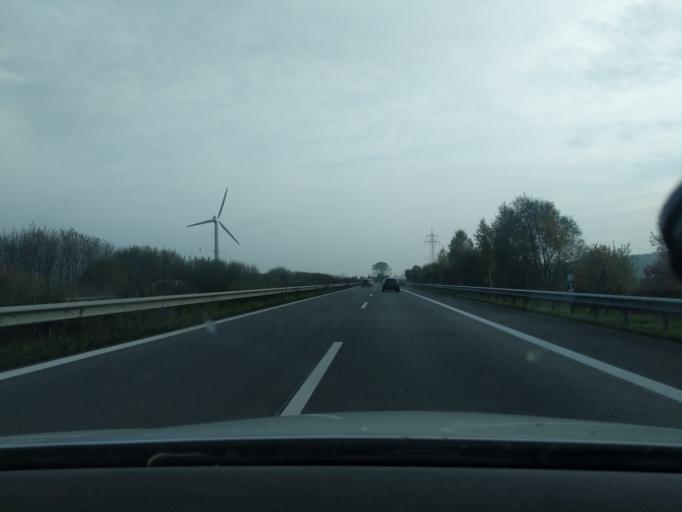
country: DE
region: Lower Saxony
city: Agathenburg
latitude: 53.5613
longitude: 9.5574
